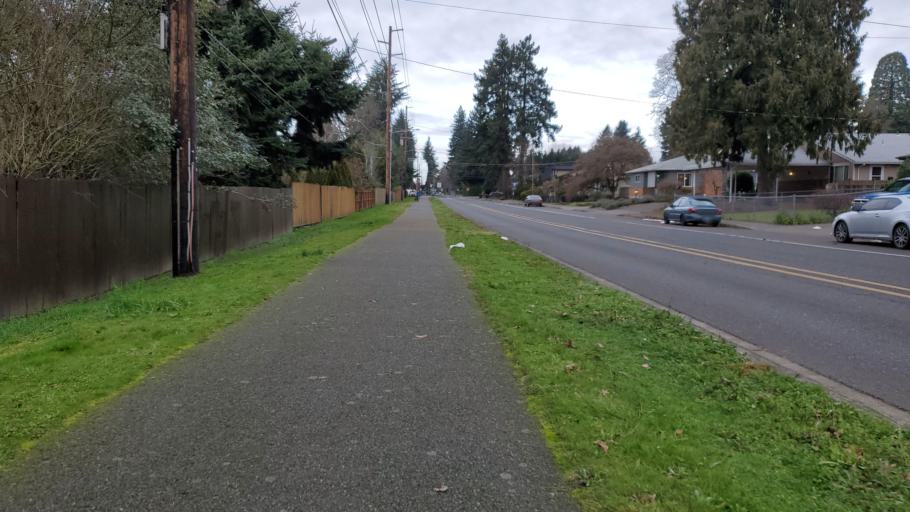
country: US
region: Oregon
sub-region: Clackamas County
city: Gladstone
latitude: 45.3852
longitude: -122.6039
